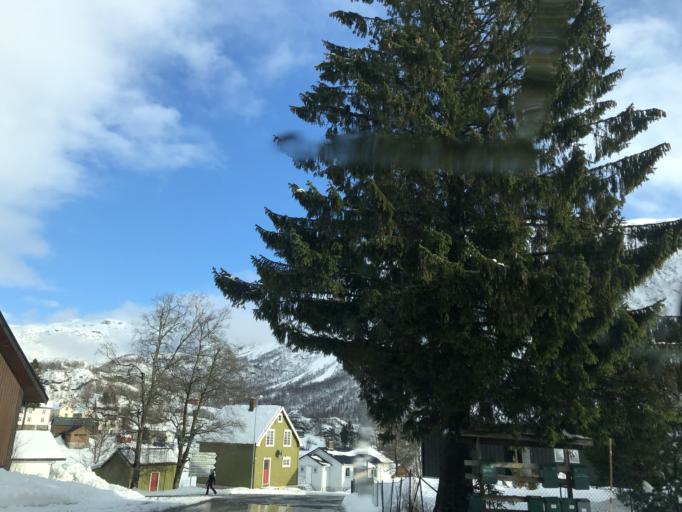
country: NO
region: Hordaland
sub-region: Odda
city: Odda
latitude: 59.8331
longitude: 6.8165
